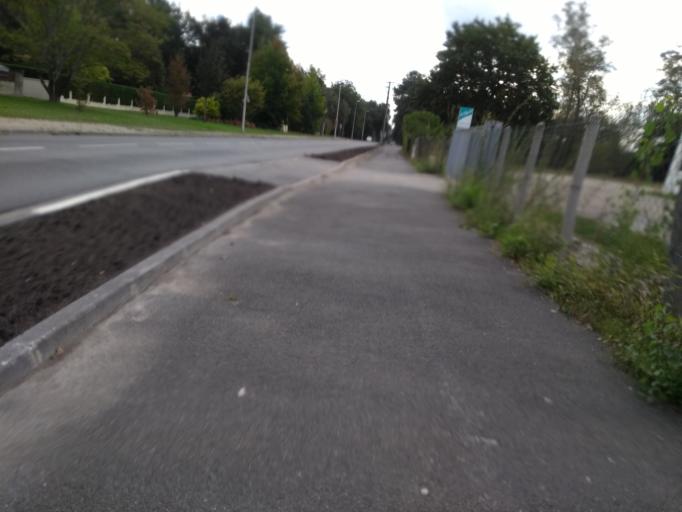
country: FR
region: Aquitaine
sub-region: Departement de la Gironde
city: Saint-Aubin-de-Medoc
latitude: 44.7668
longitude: -0.6945
